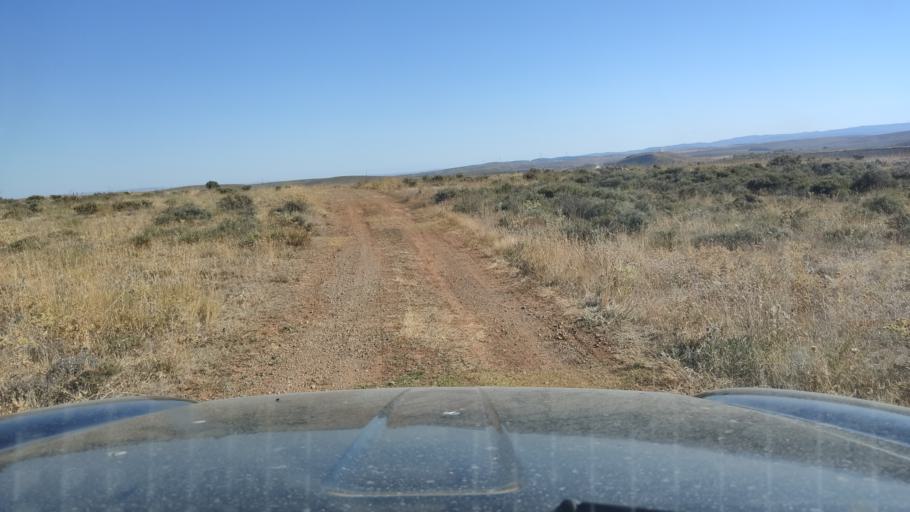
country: ES
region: Aragon
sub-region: Provincia de Teruel
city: Monforte de Moyuela
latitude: 41.0279
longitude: -1.0006
